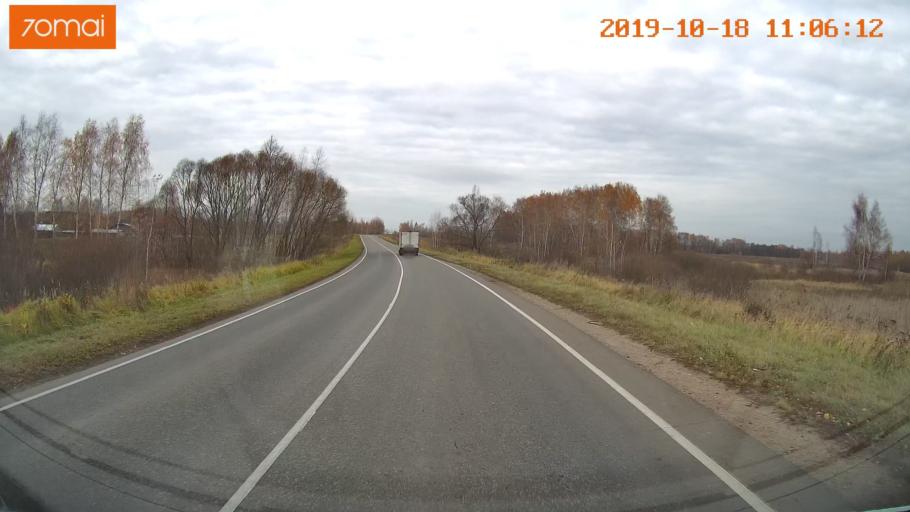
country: RU
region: Tula
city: Kimovsk
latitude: 53.9171
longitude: 38.5410
